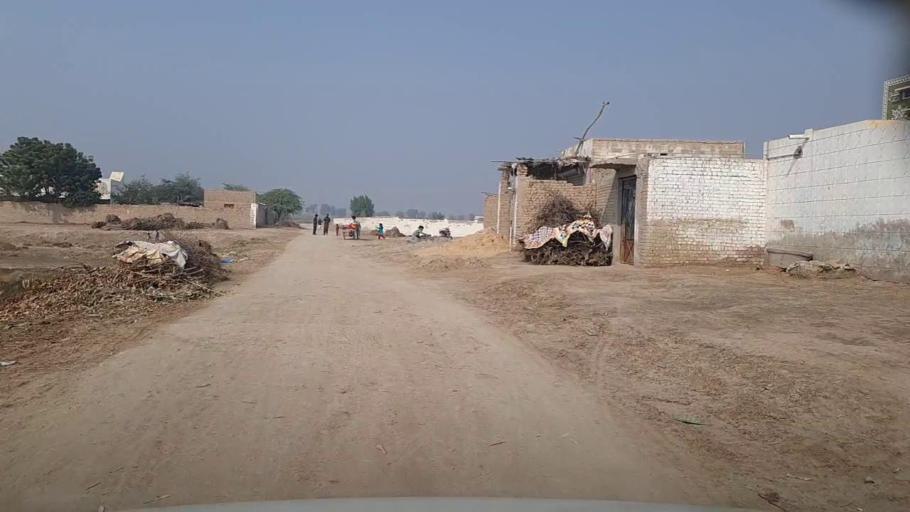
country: PK
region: Sindh
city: Setharja Old
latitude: 27.1915
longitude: 68.4733
